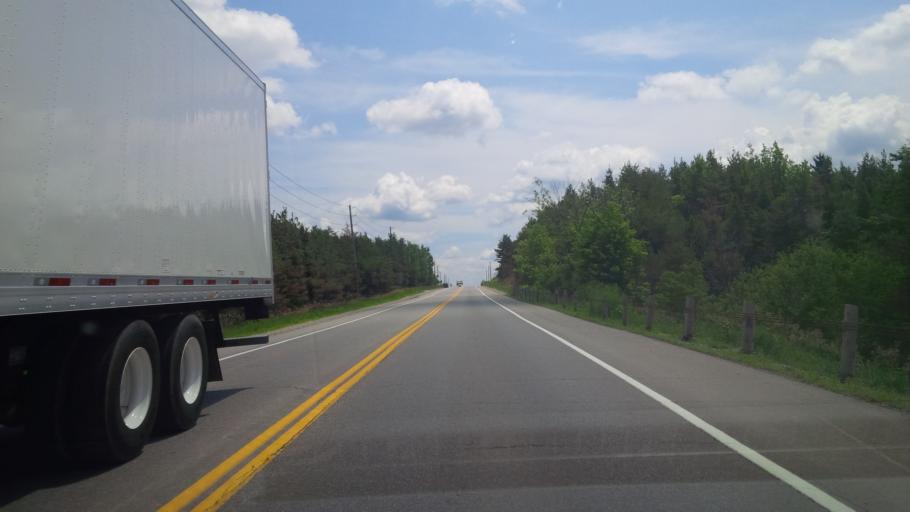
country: CA
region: Ontario
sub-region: Wellington County
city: Guelph
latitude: 43.4910
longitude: -80.1764
